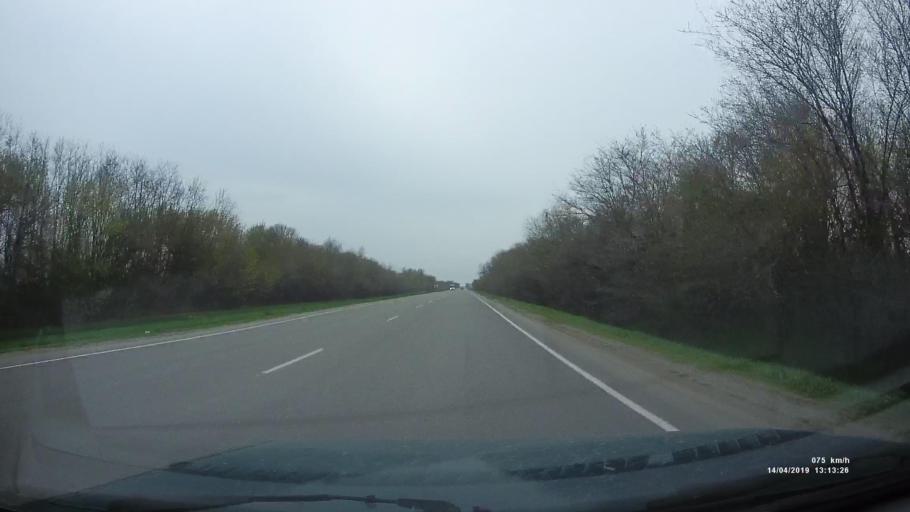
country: RU
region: Rostov
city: Kuleshovka
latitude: 47.0969
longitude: 39.6239
